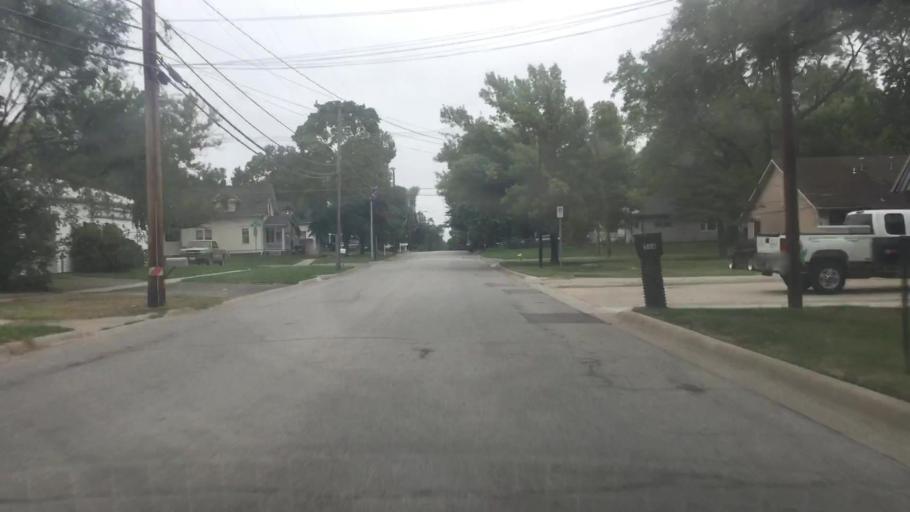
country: US
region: Kansas
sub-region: Douglas County
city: Lawrence
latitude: 38.9744
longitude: -95.2511
